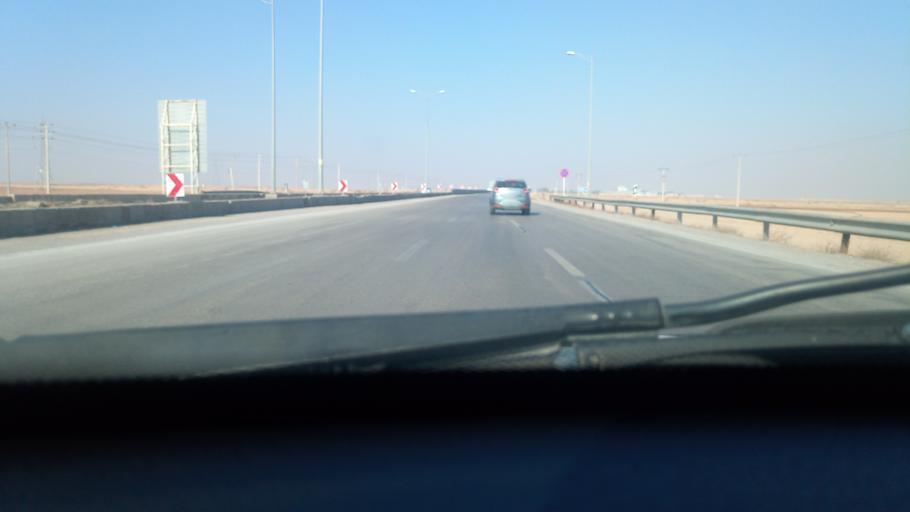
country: IR
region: Razavi Khorasan
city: Chenaran
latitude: 36.8438
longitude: 58.7920
